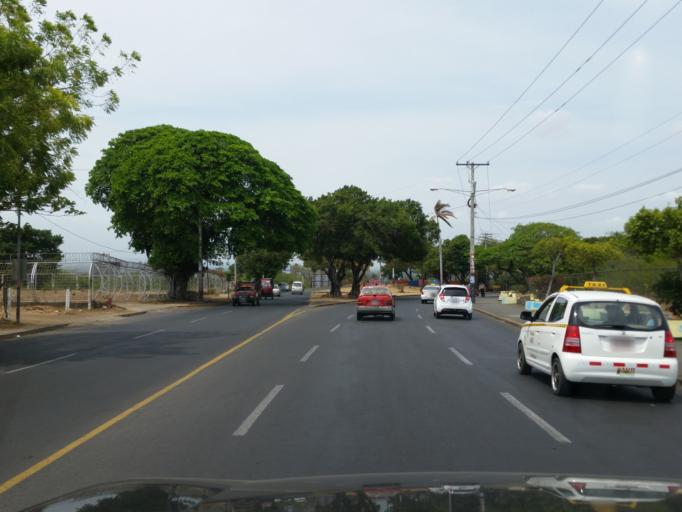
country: NI
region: Managua
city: Managua
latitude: 12.1383
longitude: -86.2682
